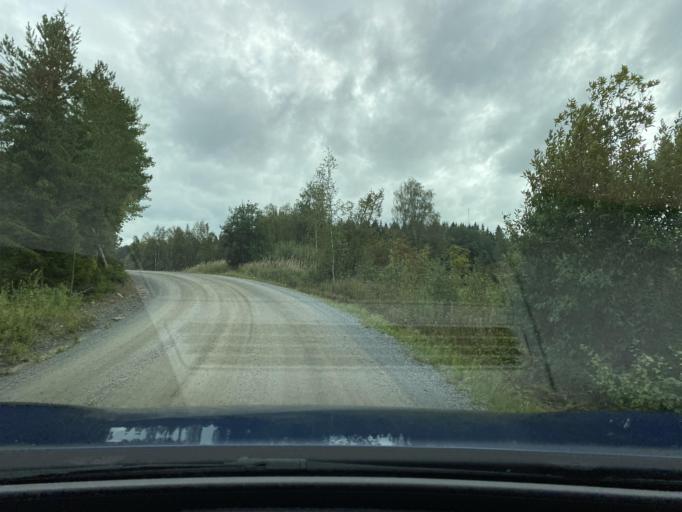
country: FI
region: Pirkanmaa
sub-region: Lounais-Pirkanmaa
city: Vammala
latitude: 61.2640
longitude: 23.0007
